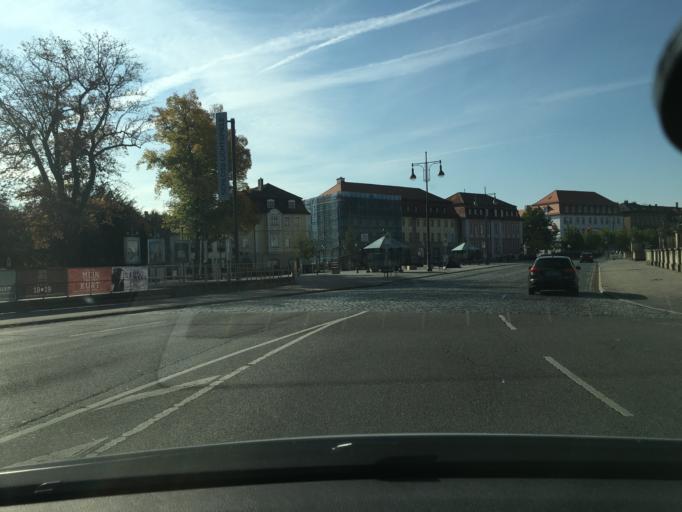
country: DE
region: Bavaria
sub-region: Regierungsbezirk Mittelfranken
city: Ansbach
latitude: 49.3029
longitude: 10.5772
